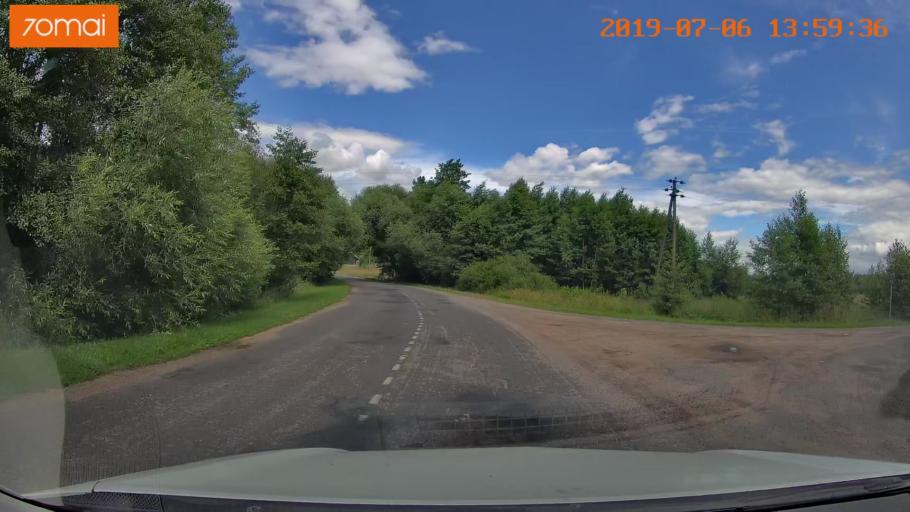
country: BY
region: Minsk
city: Ivyanyets
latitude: 53.7960
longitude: 26.8156
